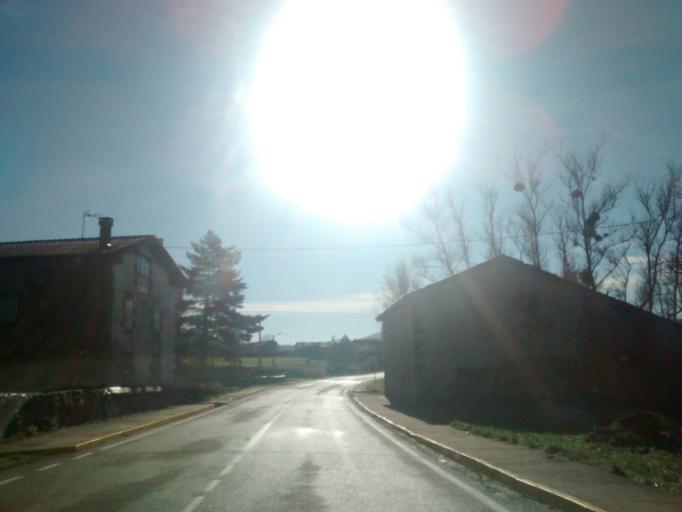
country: ES
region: Cantabria
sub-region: Provincia de Cantabria
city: San Pedro del Romeral
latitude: 42.9852
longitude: -3.8149
